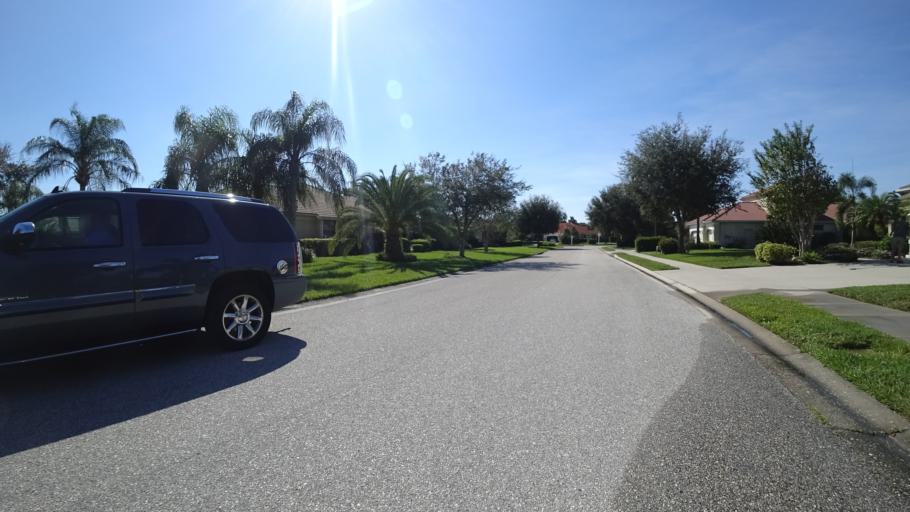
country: US
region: Florida
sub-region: Sarasota County
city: The Meadows
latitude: 27.4237
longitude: -82.4044
